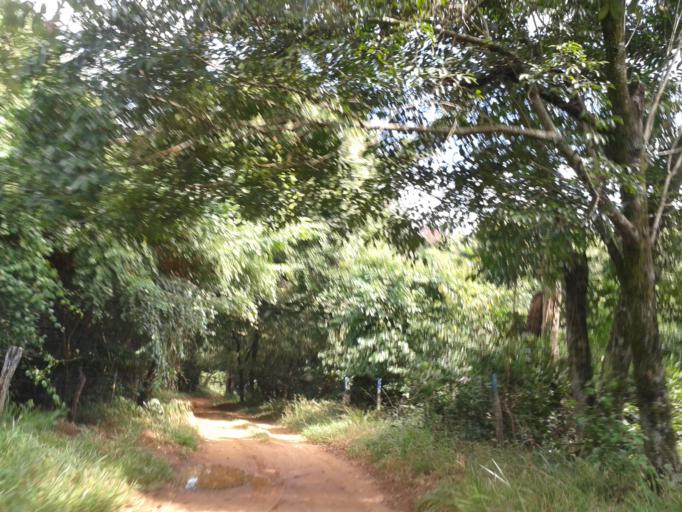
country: BR
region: Minas Gerais
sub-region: Campina Verde
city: Campina Verde
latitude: -19.3920
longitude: -49.6360
